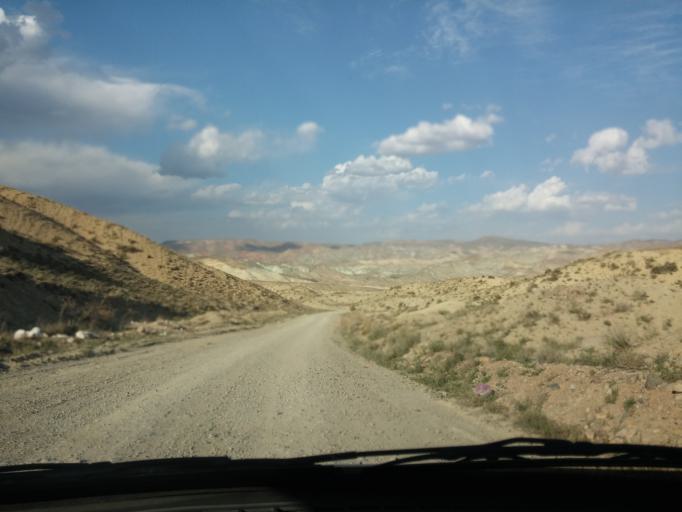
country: IR
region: Tehran
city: Damavand
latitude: 35.5358
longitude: 52.2071
